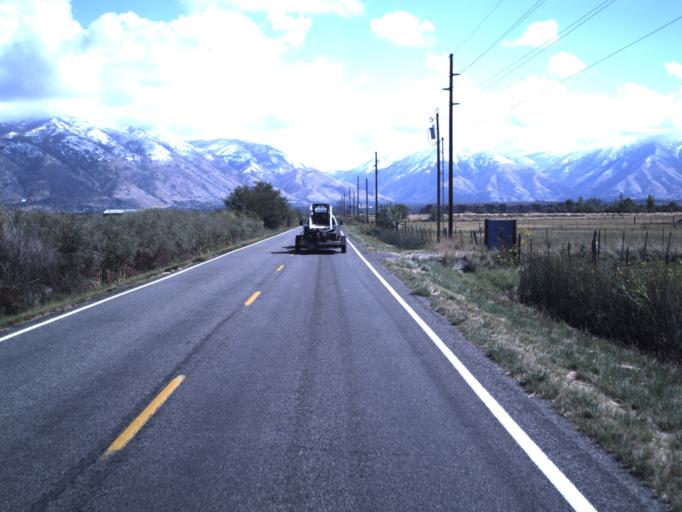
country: US
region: Utah
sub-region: Utah County
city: Spanish Fork
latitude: 40.1585
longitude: -111.6724
